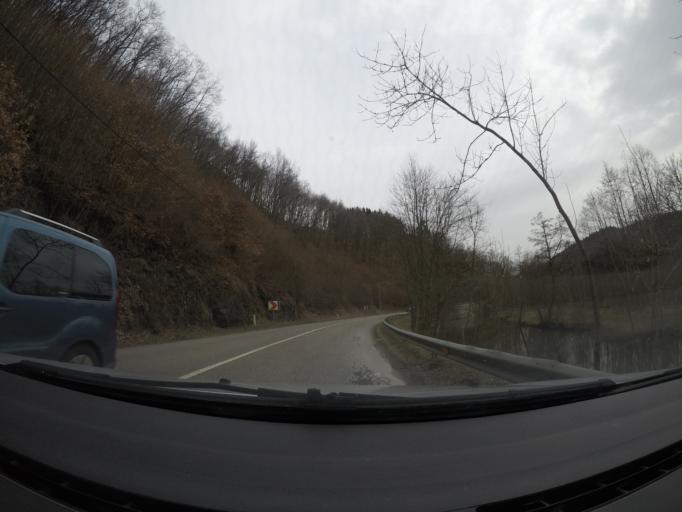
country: BE
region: Wallonia
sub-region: Province du Luxembourg
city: Martelange
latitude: 49.8351
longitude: 5.7300
